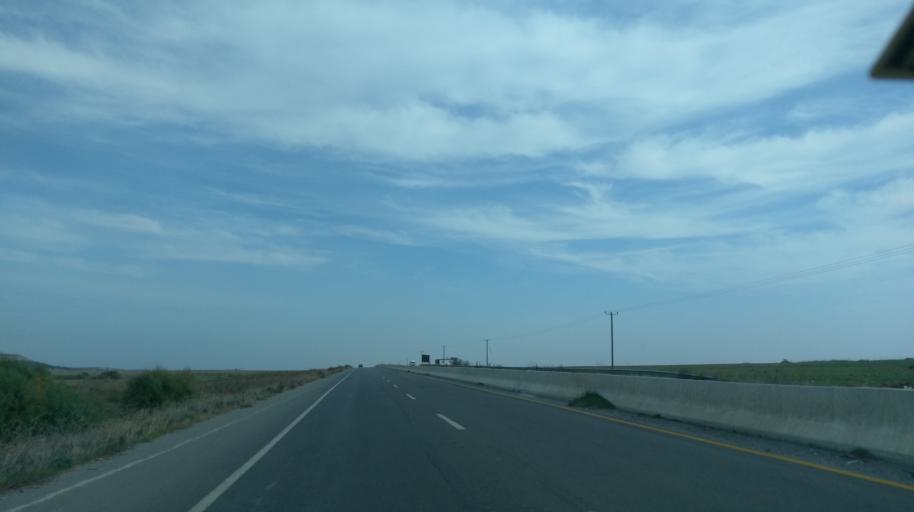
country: CY
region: Lefkosia
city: Mammari
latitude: 35.2138
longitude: 33.1919
